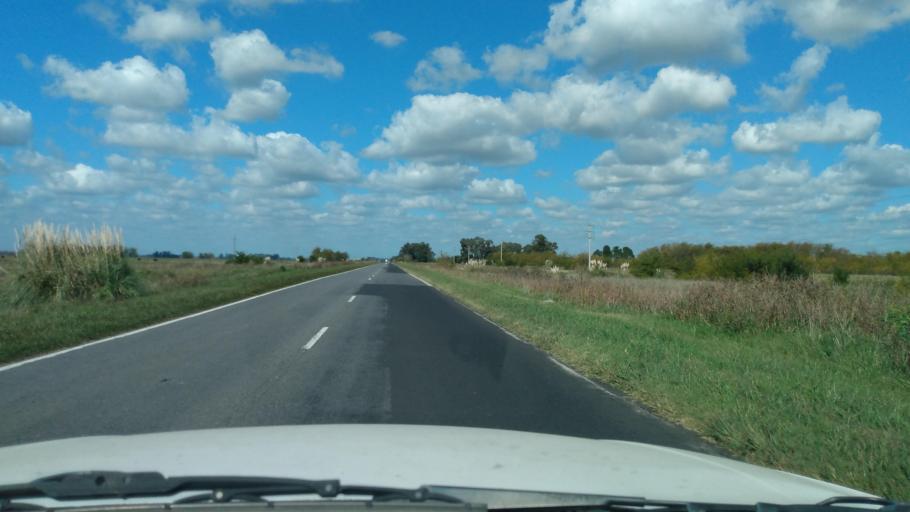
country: AR
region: Buenos Aires
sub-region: Partido de Navarro
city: Navarro
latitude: -34.8966
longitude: -59.3357
